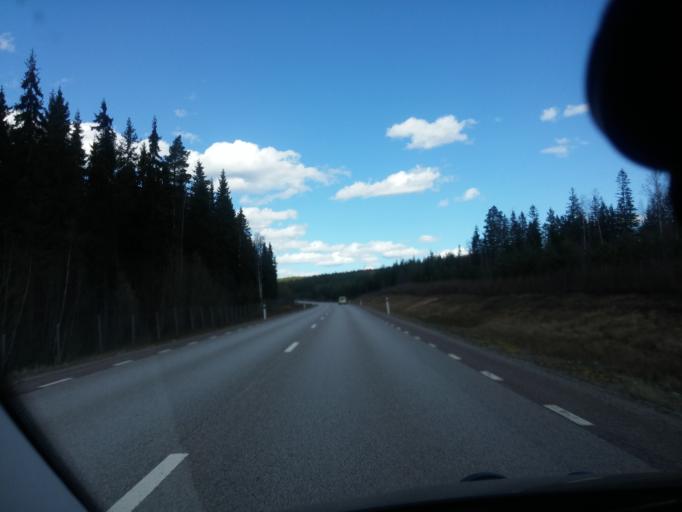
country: SE
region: Dalarna
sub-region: Faluns Kommun
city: Falun
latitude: 60.6556
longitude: 15.6445
